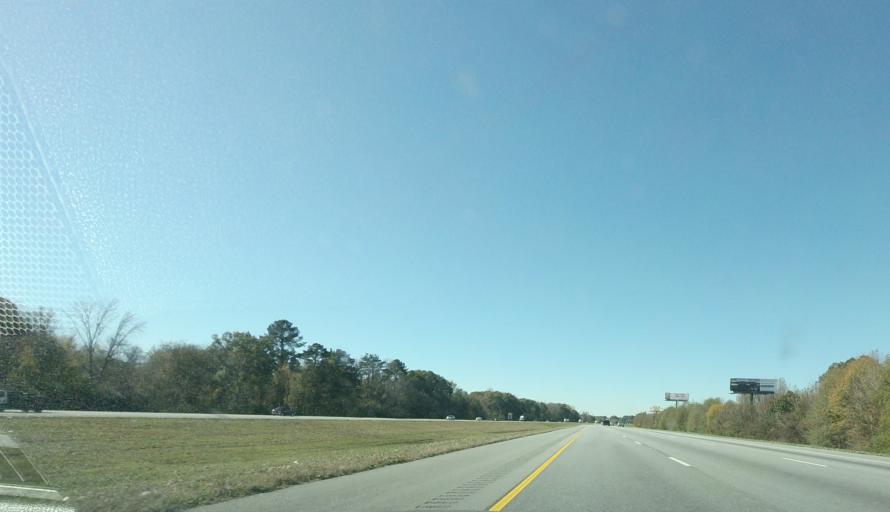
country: US
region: Alabama
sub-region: Calhoun County
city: Oxford
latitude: 33.6076
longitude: -85.8046
